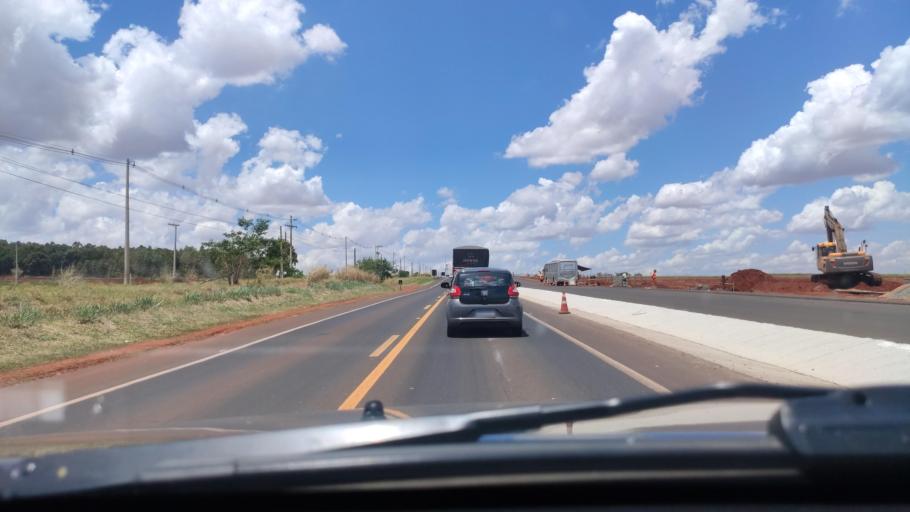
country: BR
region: Sao Paulo
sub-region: Jau
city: Jau
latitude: -22.2440
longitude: -48.5417
